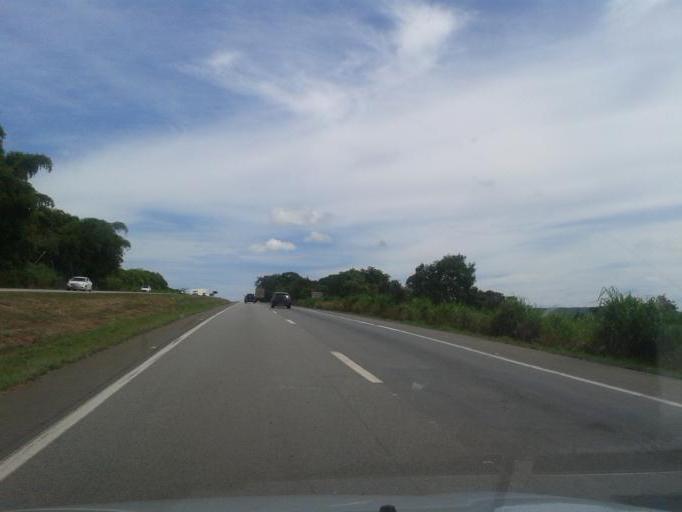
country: BR
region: Goias
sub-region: Hidrolandia
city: Hidrolandia
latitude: -17.1205
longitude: -49.2111
